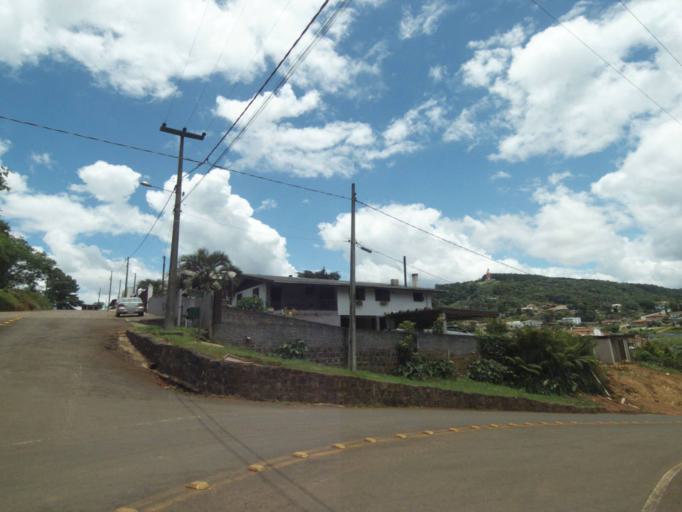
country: BR
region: Parana
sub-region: Uniao Da Vitoria
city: Uniao da Vitoria
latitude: -26.1569
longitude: -51.5519
